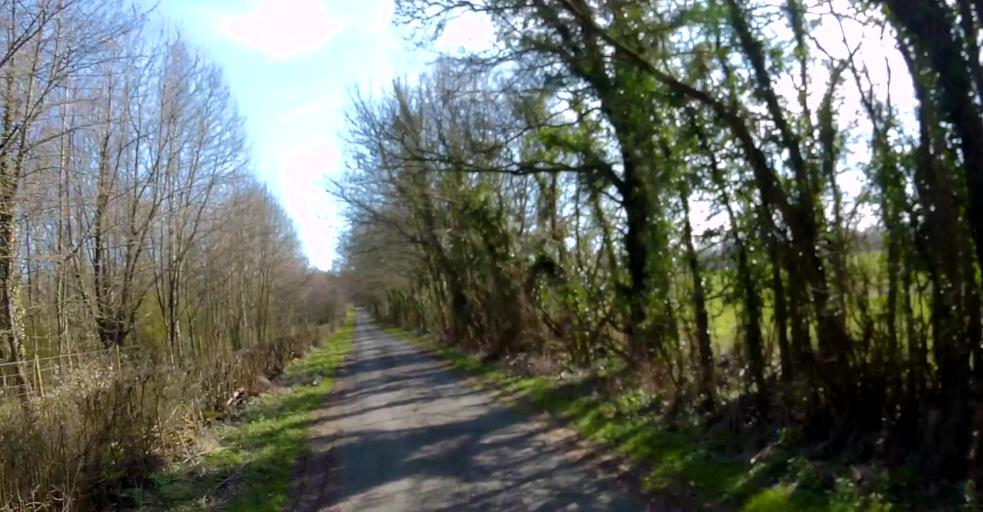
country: GB
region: England
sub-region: Hampshire
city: Four Marks
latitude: 51.1789
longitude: -1.0654
